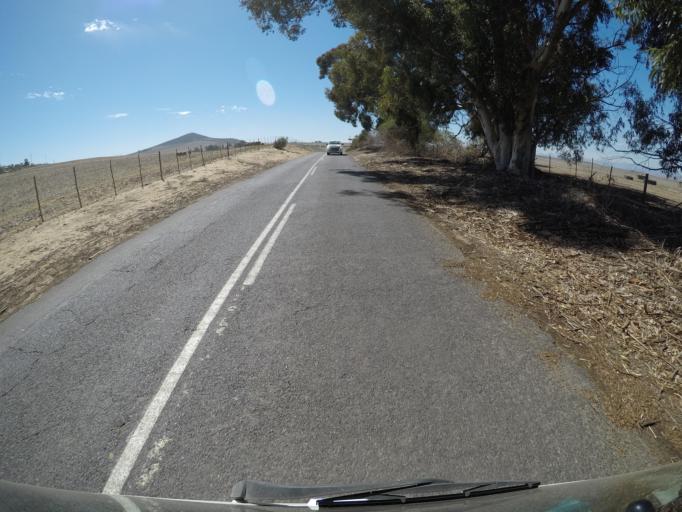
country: ZA
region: Western Cape
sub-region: City of Cape Town
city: Sunset Beach
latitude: -33.7471
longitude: 18.5587
